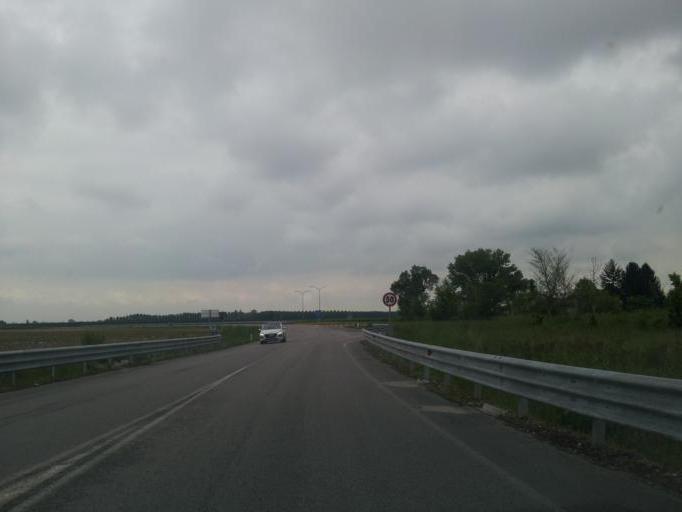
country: IT
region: Friuli Venezia Giulia
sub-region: Provincia di Udine
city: Varmo
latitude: 45.9084
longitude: 13.0032
